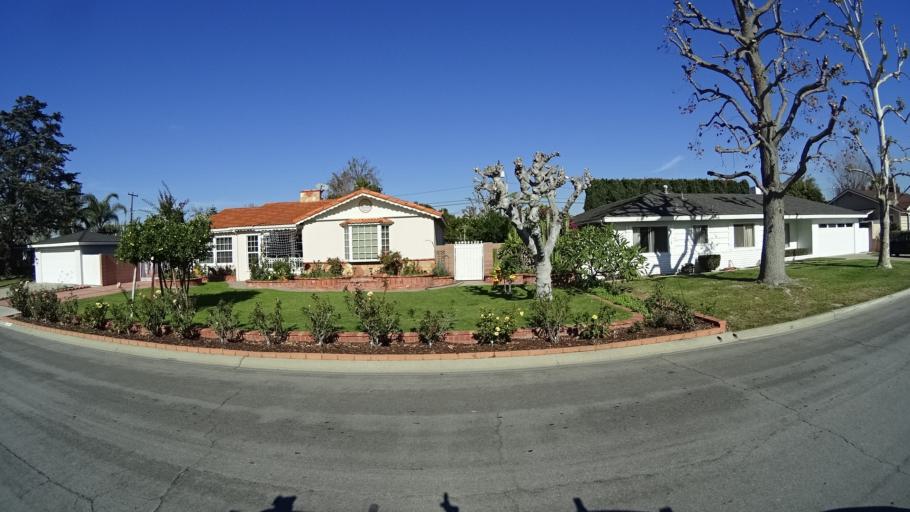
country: US
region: California
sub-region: Orange County
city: Garden Grove
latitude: 33.7847
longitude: -117.9347
